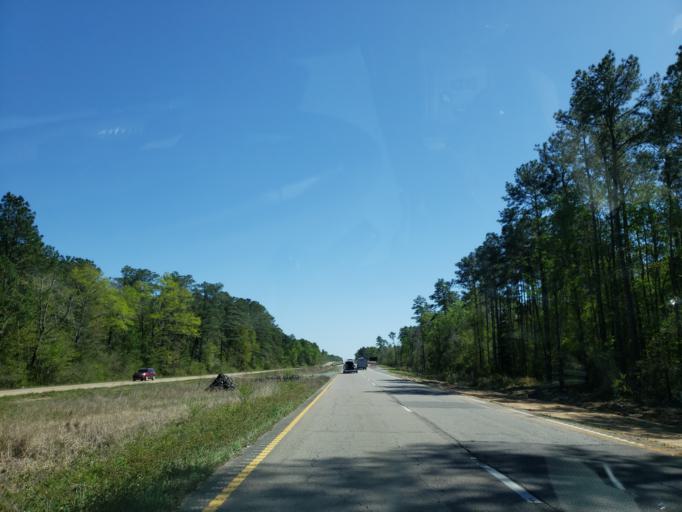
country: US
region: Mississippi
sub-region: Lamar County
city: Purvis
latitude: 31.0996
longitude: -89.2154
